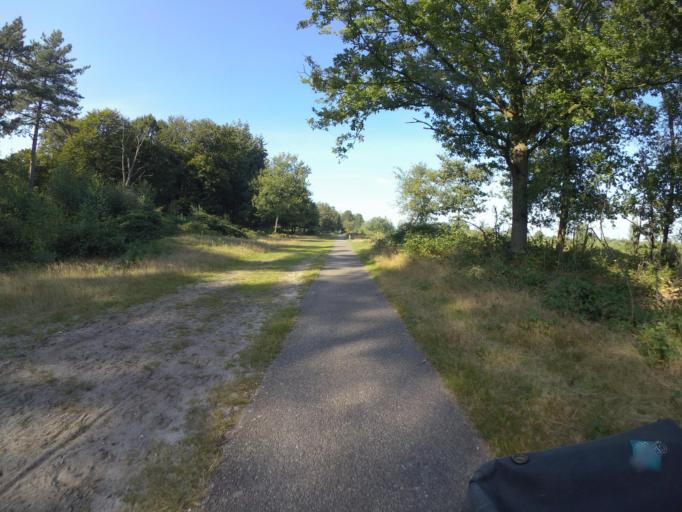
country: NL
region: North Brabant
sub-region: Gemeente Uden
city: Uden
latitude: 51.6967
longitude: 5.6220
